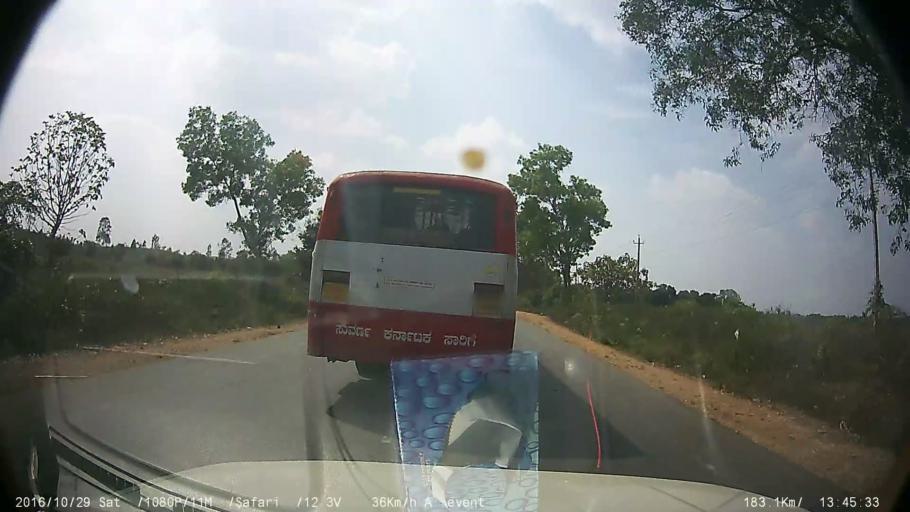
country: IN
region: Karnataka
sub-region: Mysore
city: Hunsur
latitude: 12.3122
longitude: 76.2570
